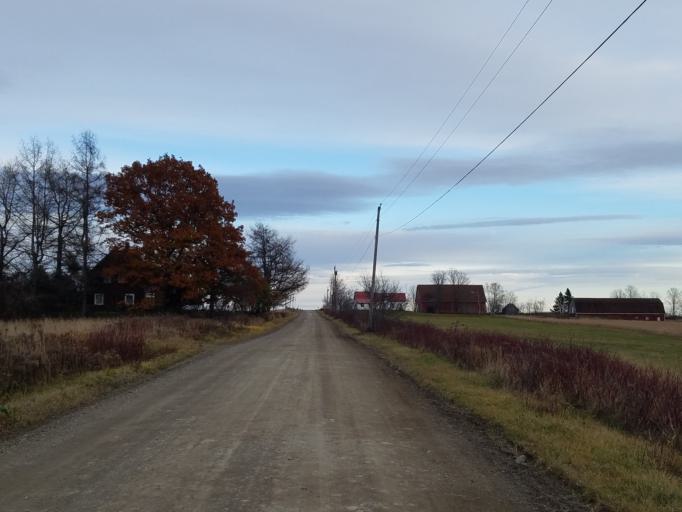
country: US
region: Maine
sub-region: Aroostook County
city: Caribou
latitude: 46.8437
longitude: -68.2326
